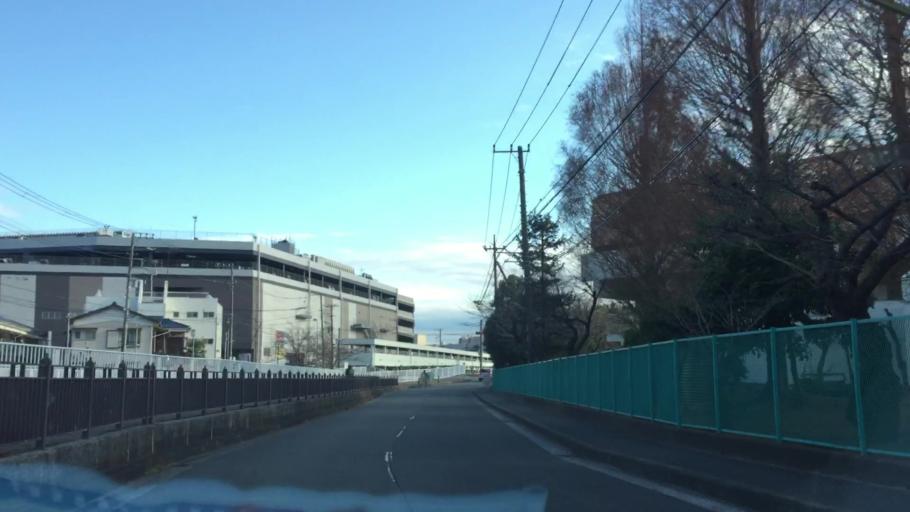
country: JP
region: Kanagawa
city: Zushi
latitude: 35.3421
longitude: 139.6186
